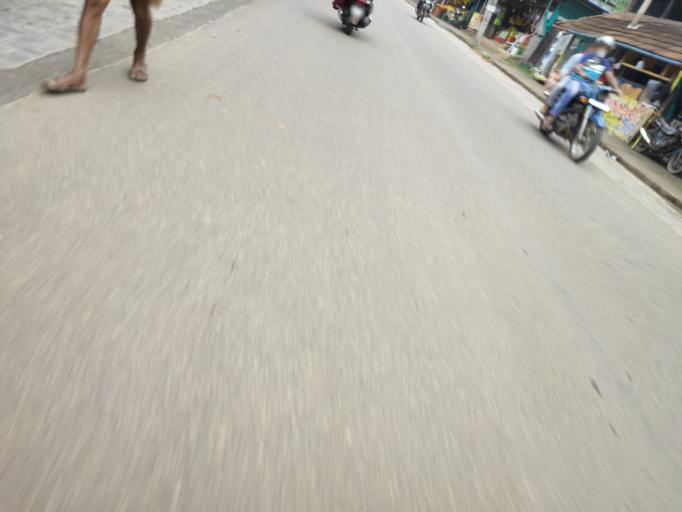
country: IN
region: Kerala
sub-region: Malappuram
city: Manjeri
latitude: 11.1907
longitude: 76.2582
